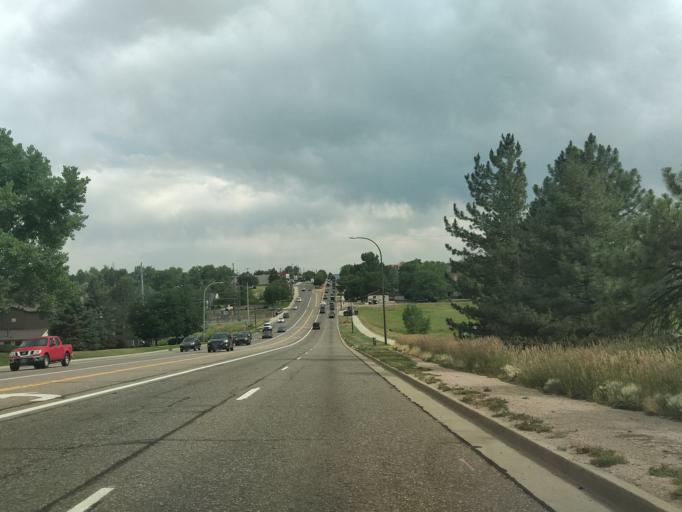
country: US
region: Colorado
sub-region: Jefferson County
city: Lakewood
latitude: 39.7030
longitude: -105.0816
